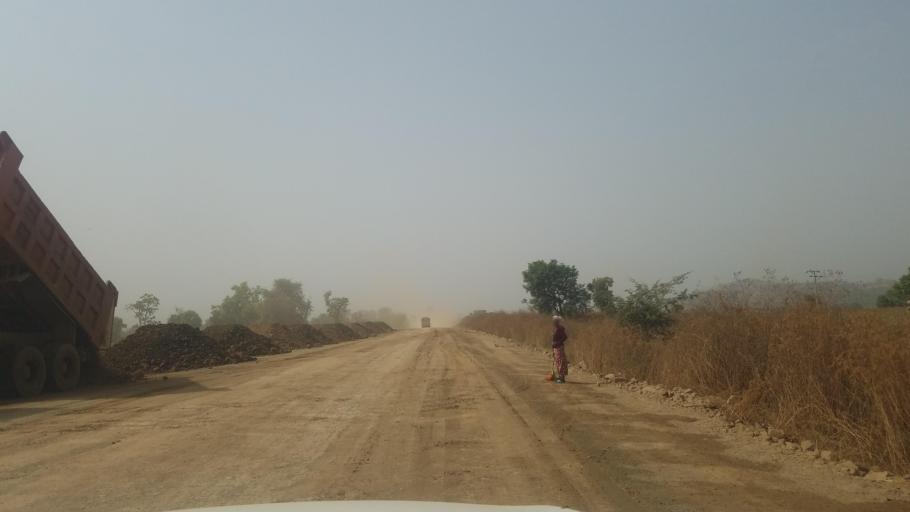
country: ET
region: Amhara
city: Bure
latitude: 10.9385
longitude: 36.4726
